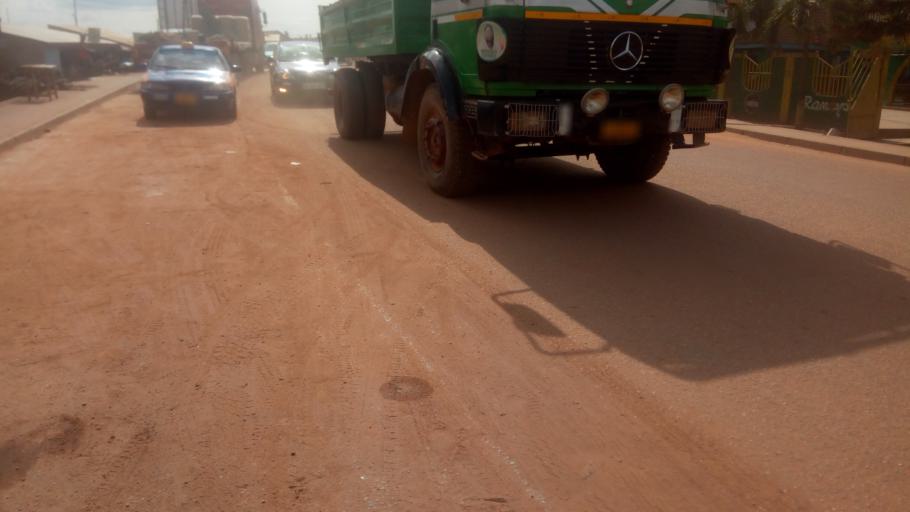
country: GH
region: Ashanti
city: Obuasi
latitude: 6.2112
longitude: -1.6887
